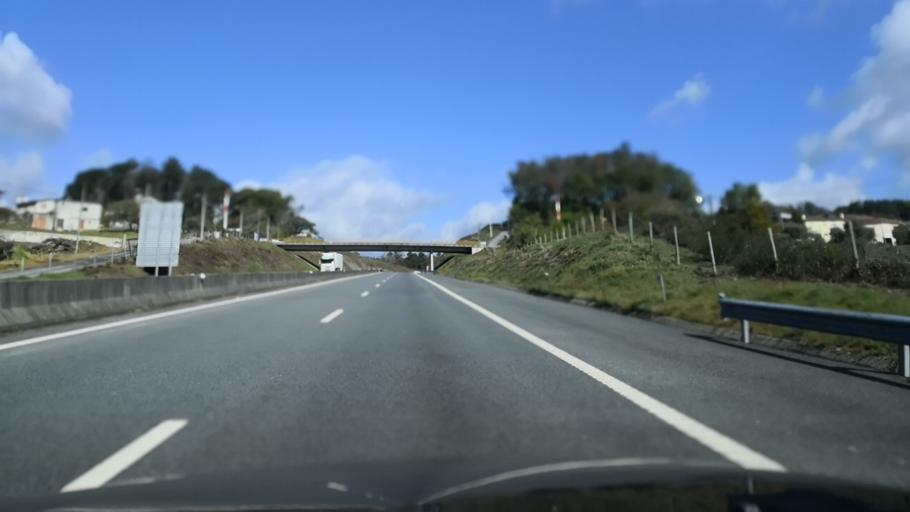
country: PT
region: Viseu
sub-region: Viseu
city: Viseu
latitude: 40.6432
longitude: -7.9625
